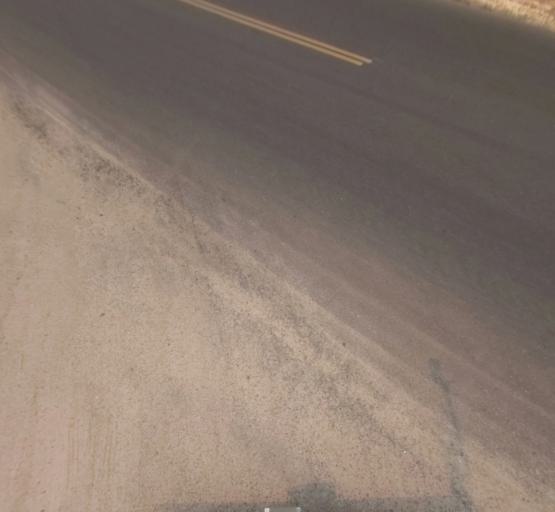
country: US
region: California
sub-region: Madera County
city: Madera Acres
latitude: 37.0212
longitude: -120.0646
